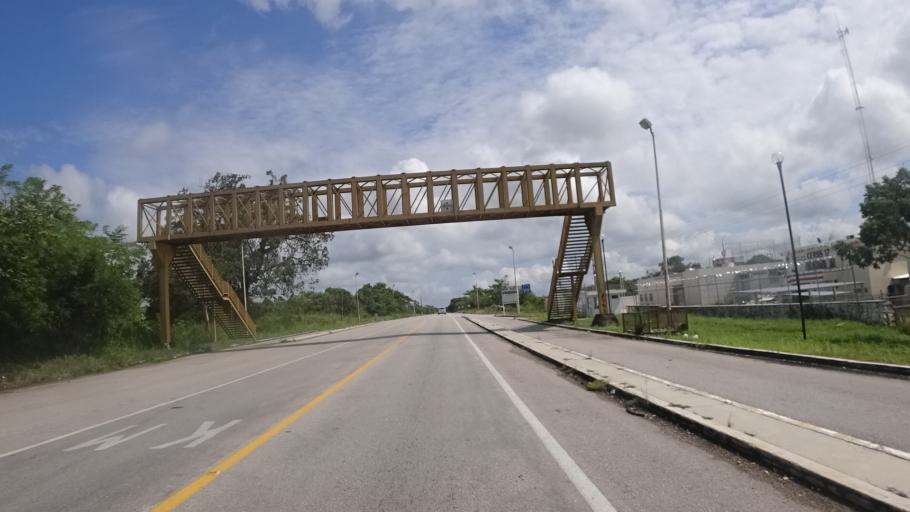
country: MX
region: Chiapas
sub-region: Catazaja
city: Catazaja
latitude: 17.6866
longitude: -92.0240
